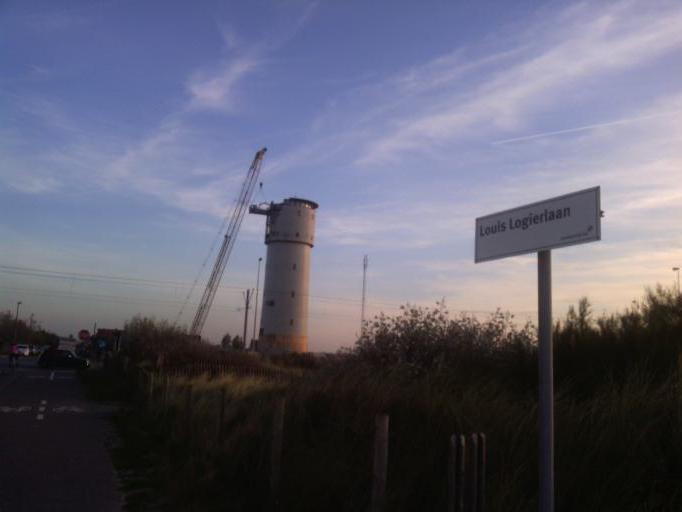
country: BE
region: Flanders
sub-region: Provincie West-Vlaanderen
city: Middelkerke
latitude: 51.1782
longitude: 2.7919
